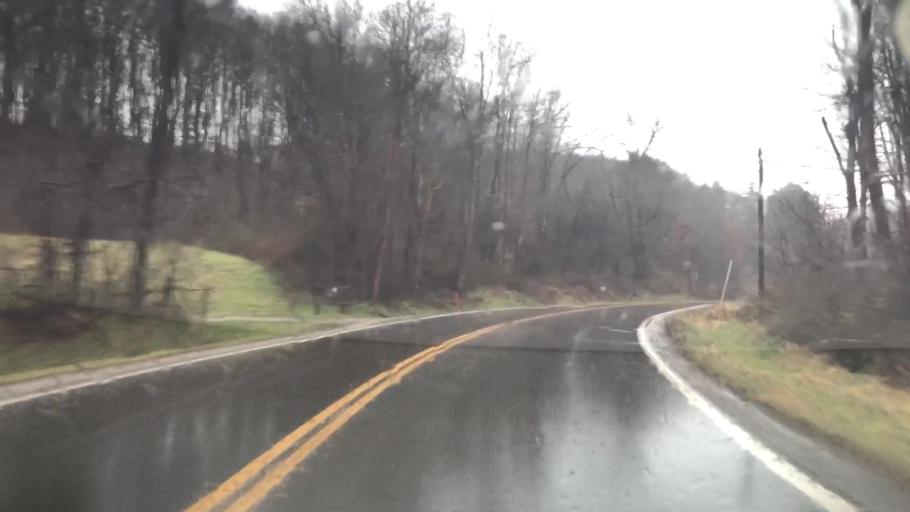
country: US
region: Ohio
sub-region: Harrison County
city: Cadiz
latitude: 40.3594
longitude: -81.0290
